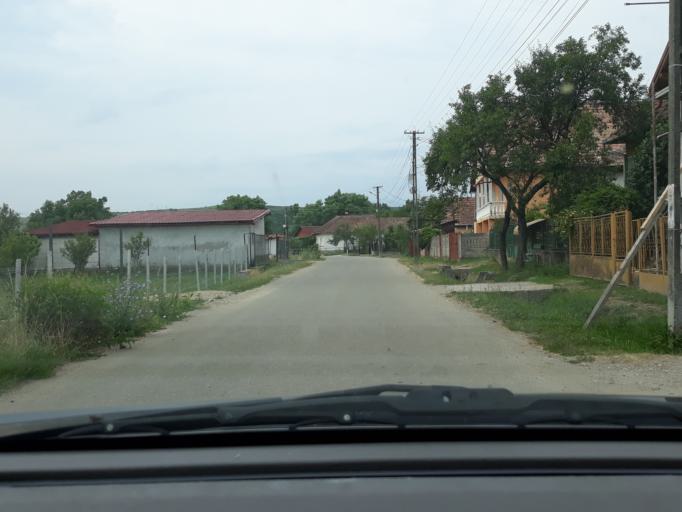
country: RO
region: Salaj
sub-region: Comuna Criseni
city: Criseni
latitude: 47.2617
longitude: 23.0650
